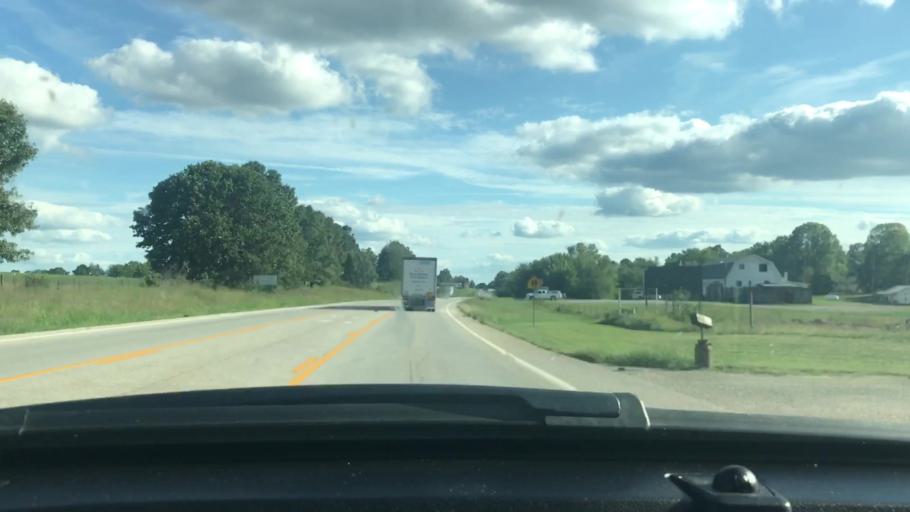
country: US
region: Missouri
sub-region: Oregon County
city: Thayer
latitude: 36.6031
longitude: -91.6441
